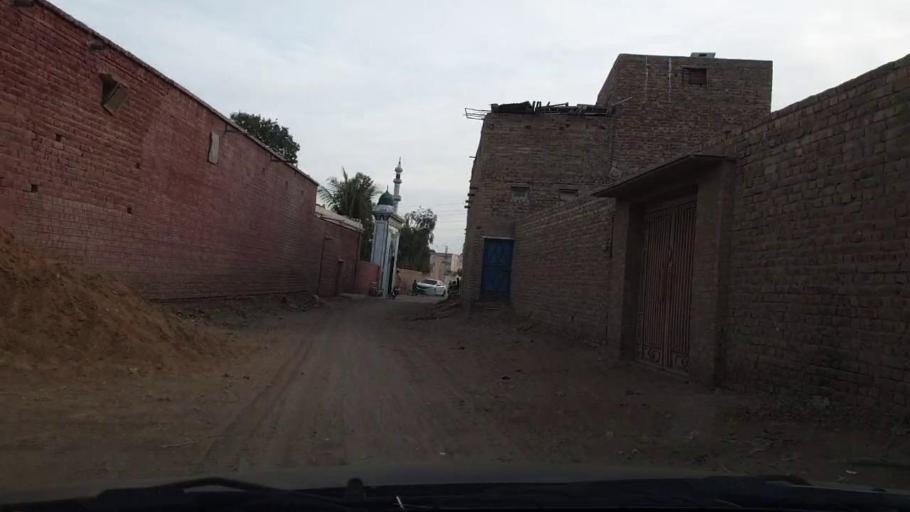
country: PK
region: Sindh
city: Khadro
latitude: 26.1480
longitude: 68.7156
